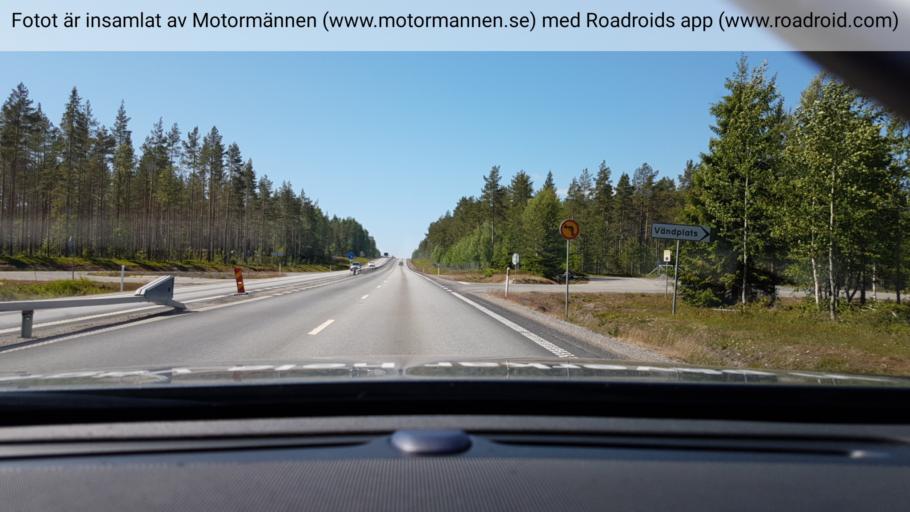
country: SE
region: Vaesterbotten
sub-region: Umea Kommun
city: Hoernefors
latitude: 63.6077
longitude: 19.7755
